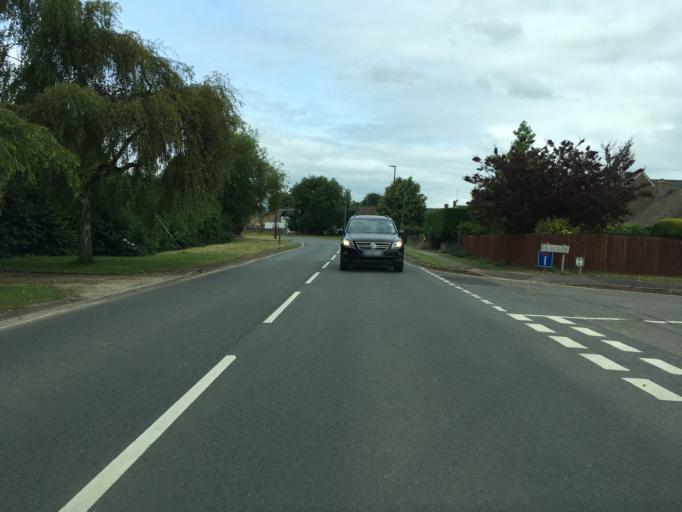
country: GB
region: England
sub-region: Gloucestershire
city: Bourton on the Water
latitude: 51.8772
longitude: -1.7442
